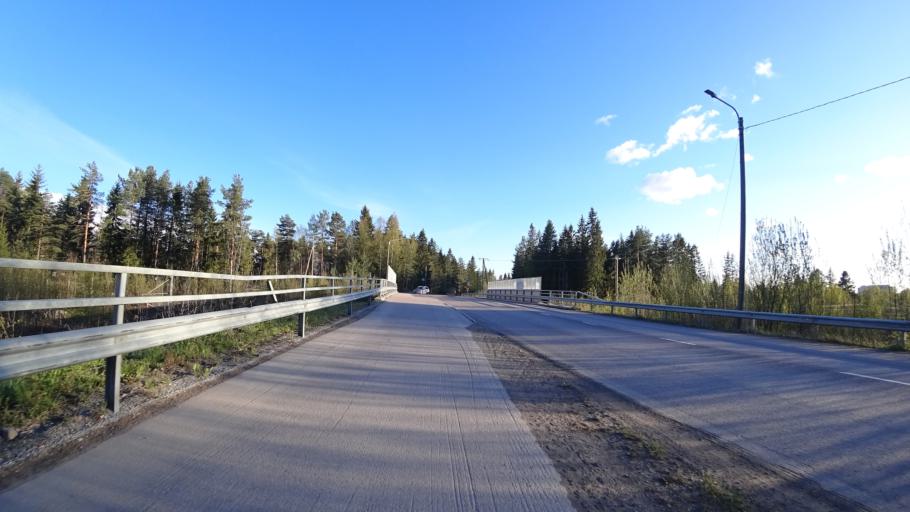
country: FI
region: Pirkanmaa
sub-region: Tampere
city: Nokia
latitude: 61.4919
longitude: 23.5334
